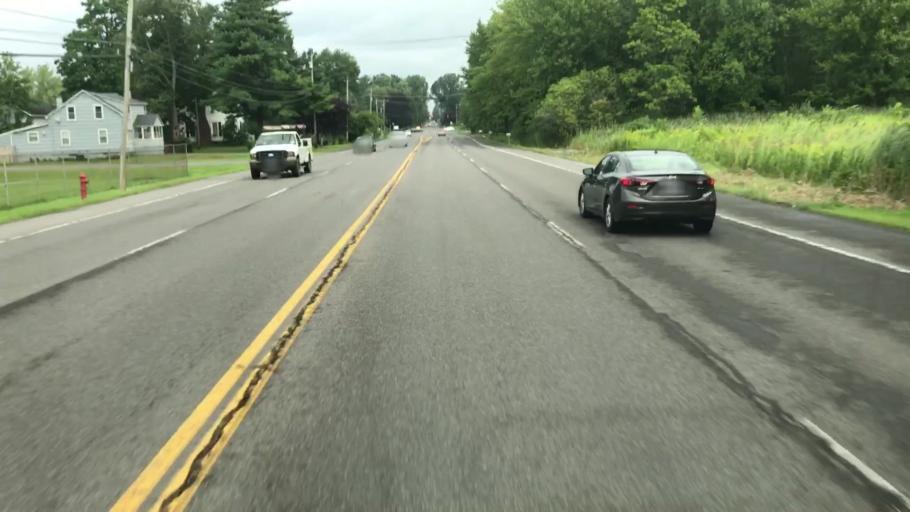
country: US
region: New York
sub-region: Onondaga County
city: Liverpool
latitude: 43.1474
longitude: -76.2073
